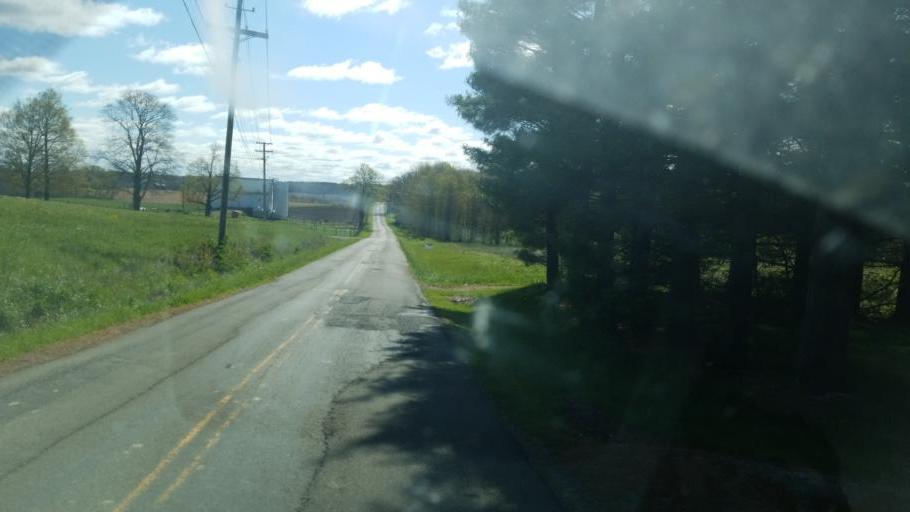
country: US
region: Ohio
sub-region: Knox County
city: Danville
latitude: 40.4238
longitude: -82.3241
